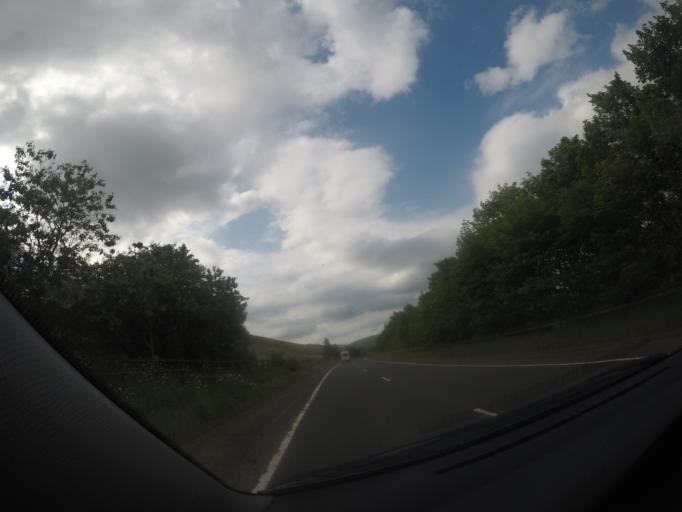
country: GB
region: Scotland
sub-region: South Lanarkshire
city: Douglas
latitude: 55.4733
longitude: -3.6935
